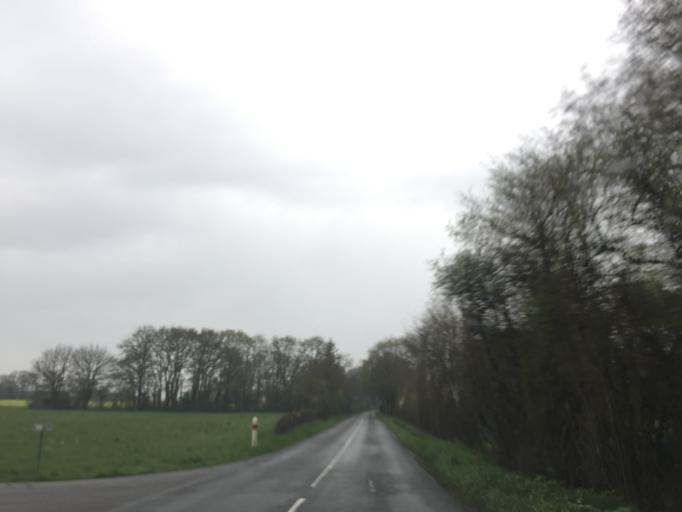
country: FR
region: Pays de la Loire
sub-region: Departement de la Loire-Atlantique
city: Suce-sur-Erdre
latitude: 47.3643
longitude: -1.5265
